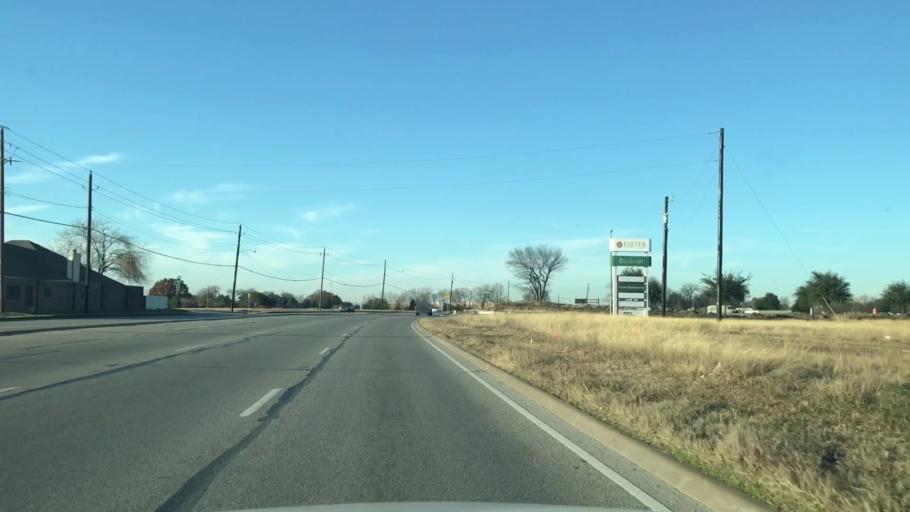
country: US
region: Texas
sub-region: Dallas County
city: Balch Springs
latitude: 32.7860
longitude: -96.6845
